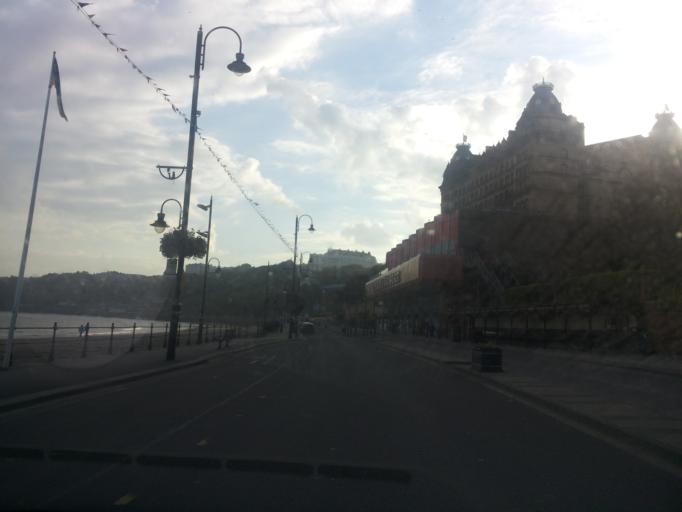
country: GB
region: England
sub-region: North Yorkshire
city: Scarborough
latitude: 54.2819
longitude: -0.3963
